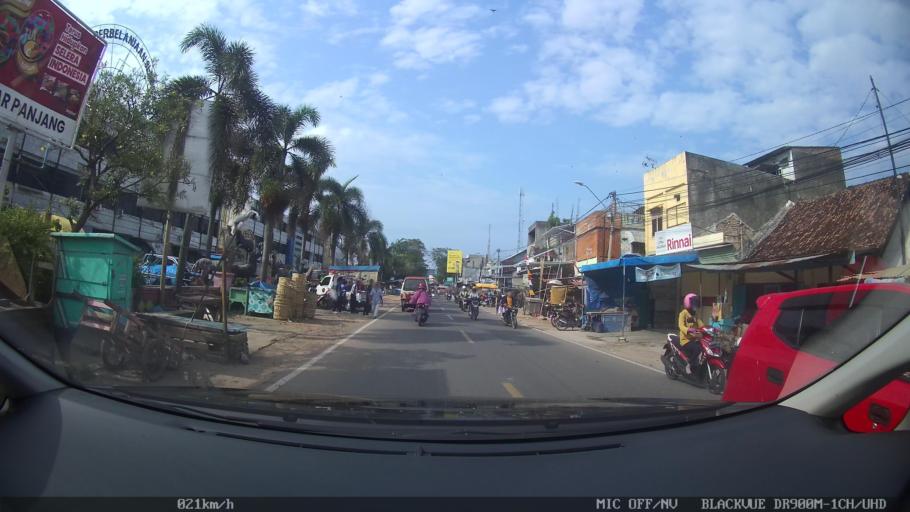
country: ID
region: Lampung
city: Panjang
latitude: -5.4712
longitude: 105.3222
